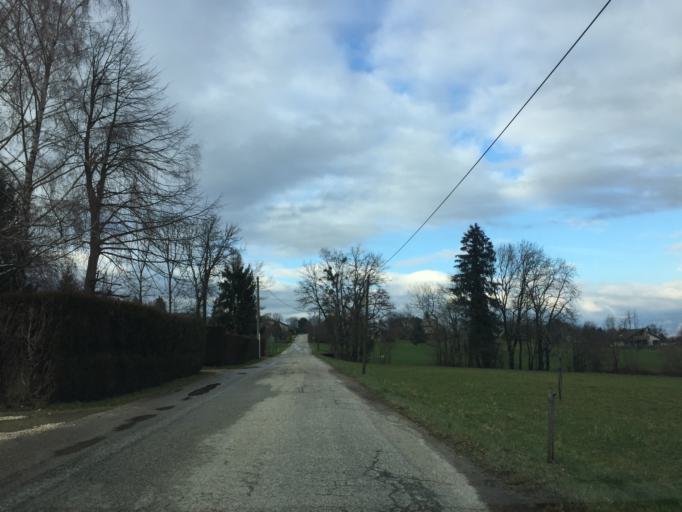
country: FR
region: Rhone-Alpes
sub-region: Departement de la Savoie
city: Vimines
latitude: 45.5427
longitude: 5.8495
